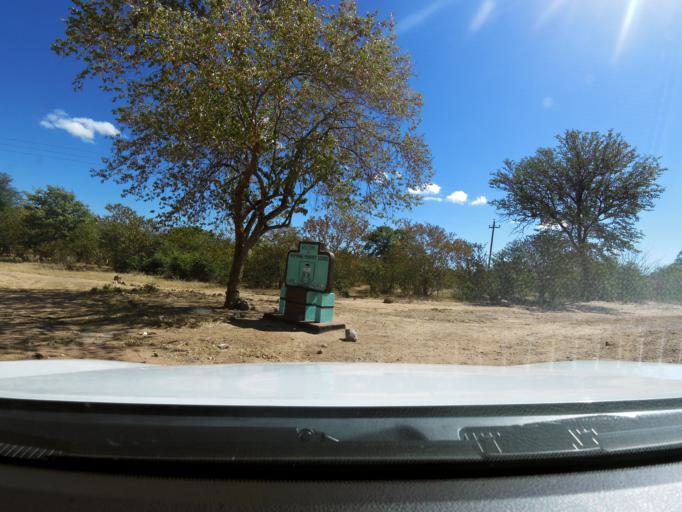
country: ZW
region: Matabeleland North
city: Kamativi Mine
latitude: -18.0966
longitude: 27.0746
